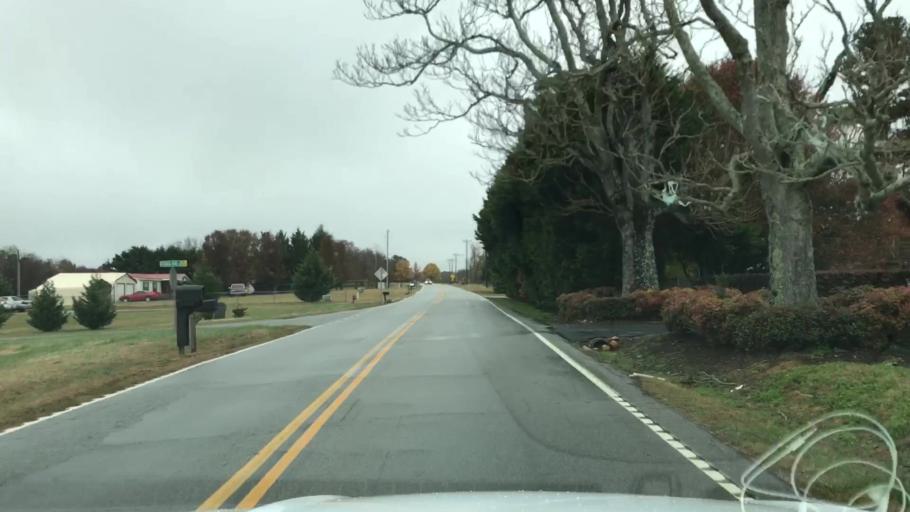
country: US
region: South Carolina
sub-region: Spartanburg County
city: Roebuck
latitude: 34.7841
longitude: -81.9165
